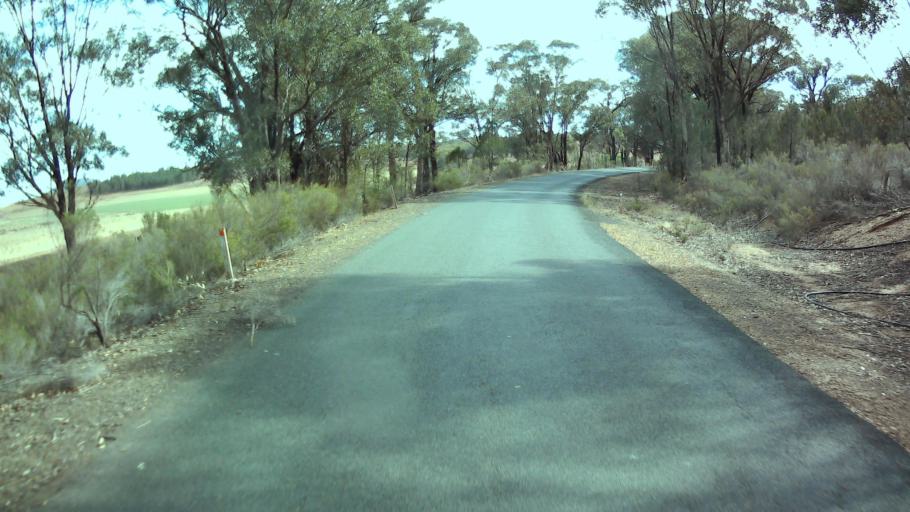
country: AU
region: New South Wales
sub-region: Weddin
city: Grenfell
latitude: -33.8443
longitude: 148.2361
